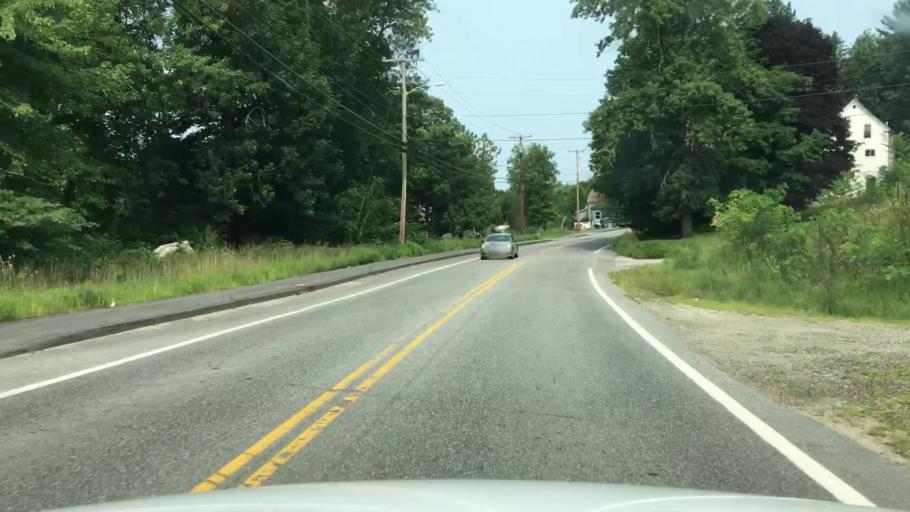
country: US
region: Maine
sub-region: Androscoggin County
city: Livermore Falls
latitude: 44.4648
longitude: -70.1814
